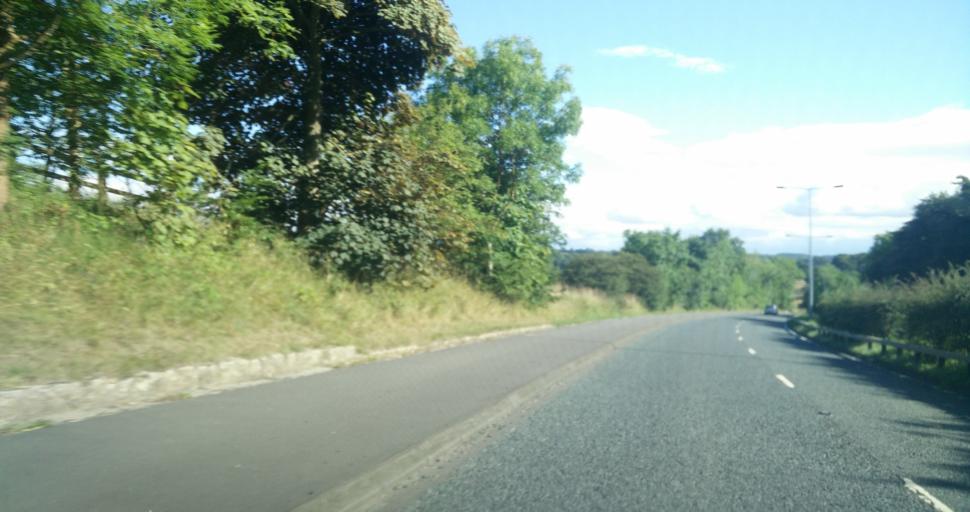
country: GB
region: England
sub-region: County Durham
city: Durham
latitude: 54.7473
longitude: -1.5896
